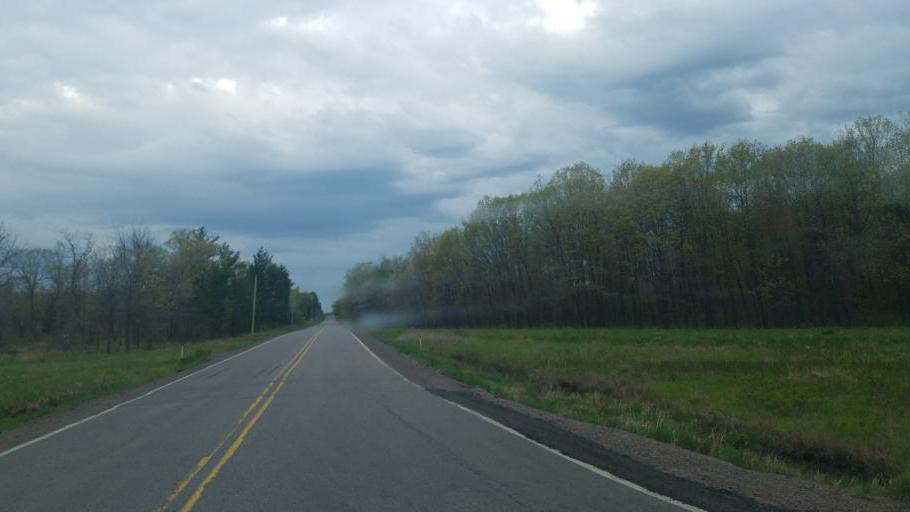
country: US
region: Wisconsin
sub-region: Wood County
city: Marshfield
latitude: 44.4092
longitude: -90.1606
